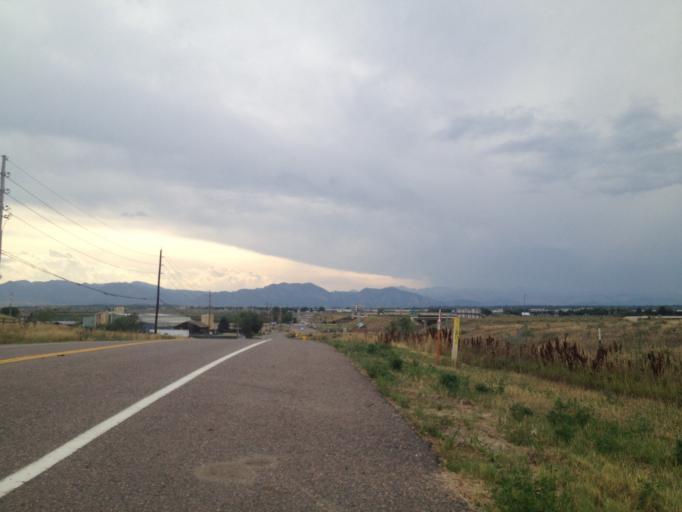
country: US
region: Colorado
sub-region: Boulder County
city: Lafayette
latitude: 39.9580
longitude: -105.0833
